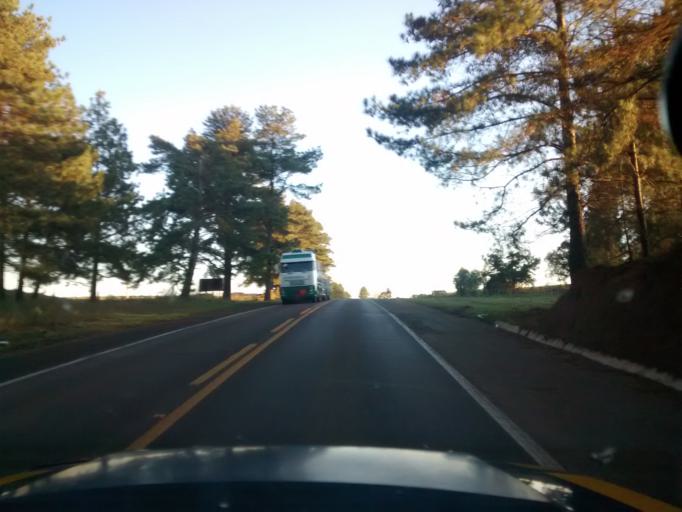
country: BR
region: Rio Grande do Sul
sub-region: Vacaria
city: Vacaria
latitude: -28.5389
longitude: -50.9695
